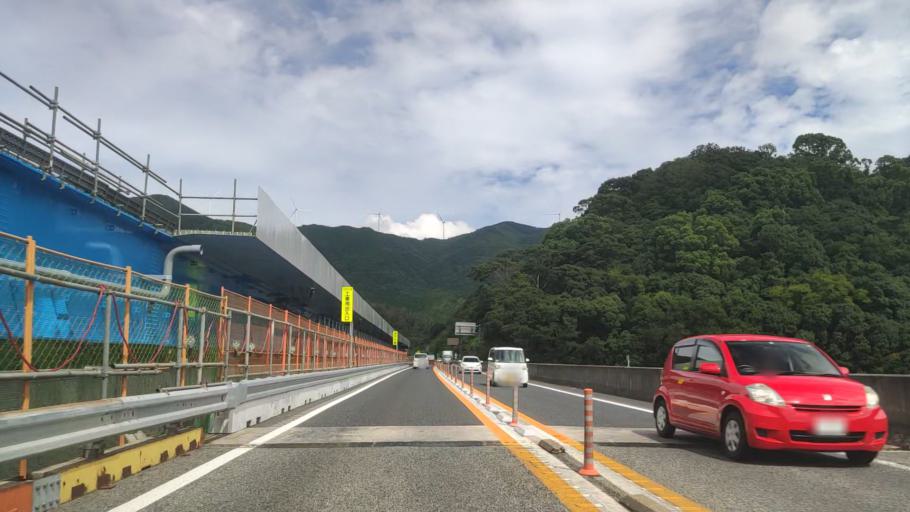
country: JP
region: Wakayama
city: Gobo
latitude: 33.9380
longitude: 135.1965
